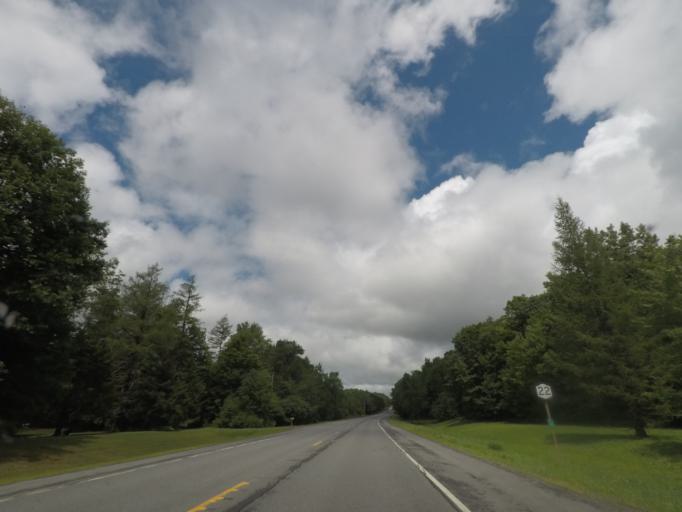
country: US
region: Massachusetts
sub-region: Berkshire County
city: Lanesborough
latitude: 42.5700
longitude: -73.3684
